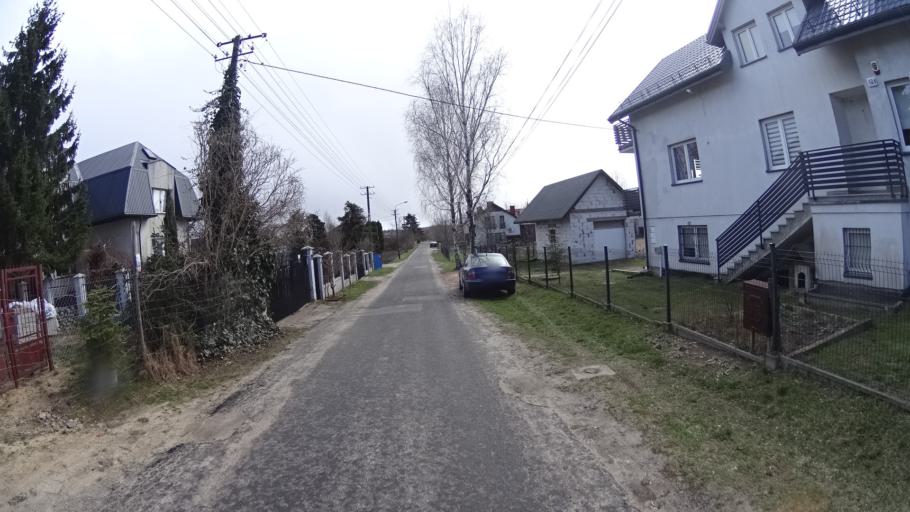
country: PL
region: Masovian Voivodeship
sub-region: Powiat warszawski zachodni
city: Jozefow
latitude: 52.2054
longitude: 20.6839
